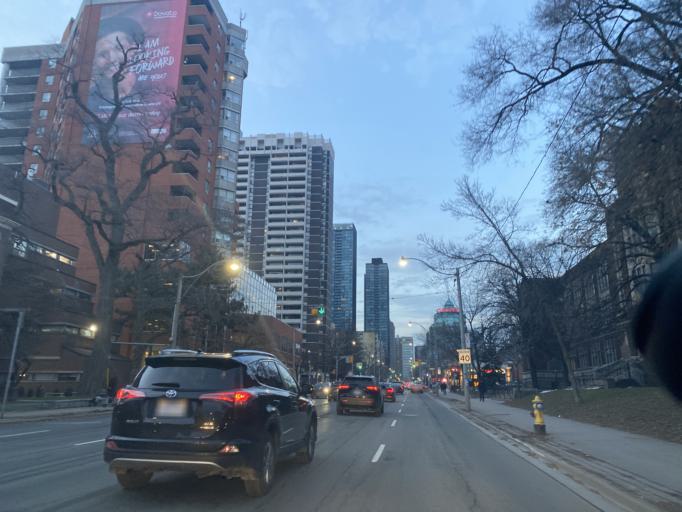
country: CA
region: Ontario
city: Toronto
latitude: 43.6654
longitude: -79.3779
